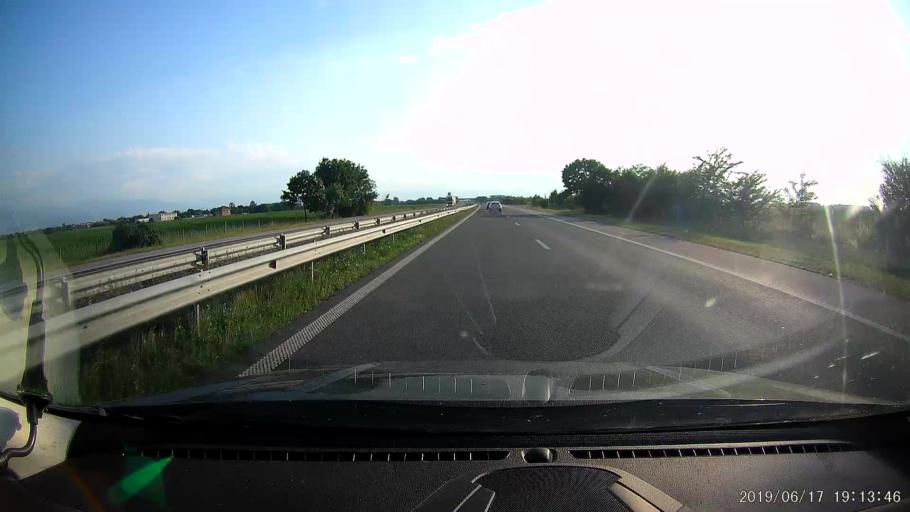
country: BG
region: Plovdiv
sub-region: Obshtina Plovdiv
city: Plovdiv
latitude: 42.2100
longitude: 24.6961
